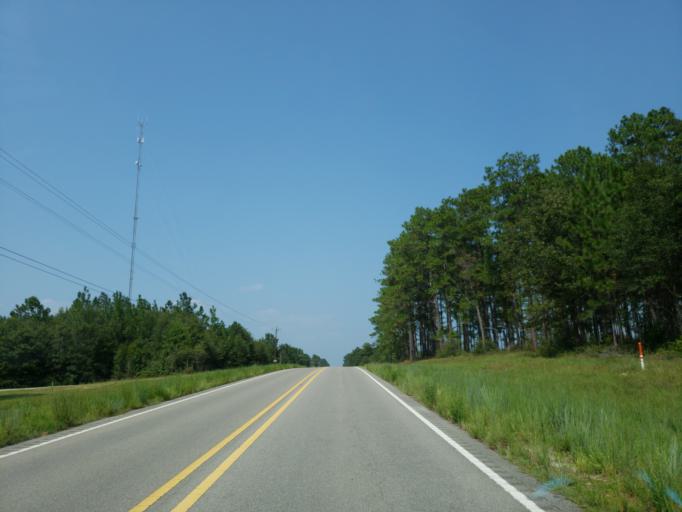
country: US
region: Mississippi
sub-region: Jones County
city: Ellisville
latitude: 31.5476
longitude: -89.2554
